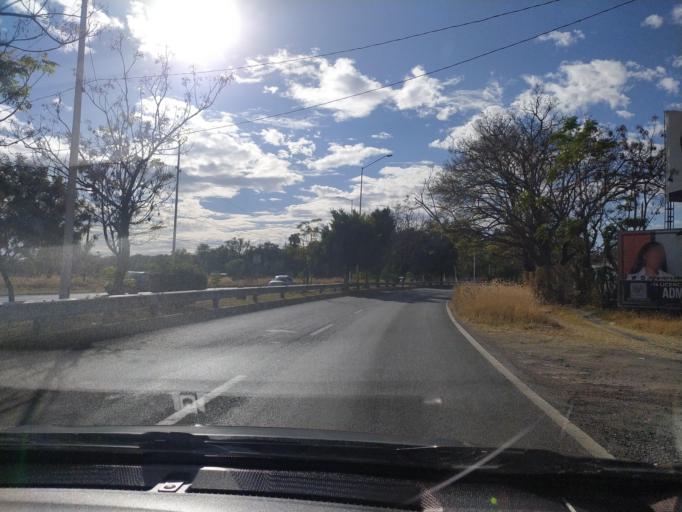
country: LA
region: Oudomxai
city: Muang La
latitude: 21.0314
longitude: 101.8322
